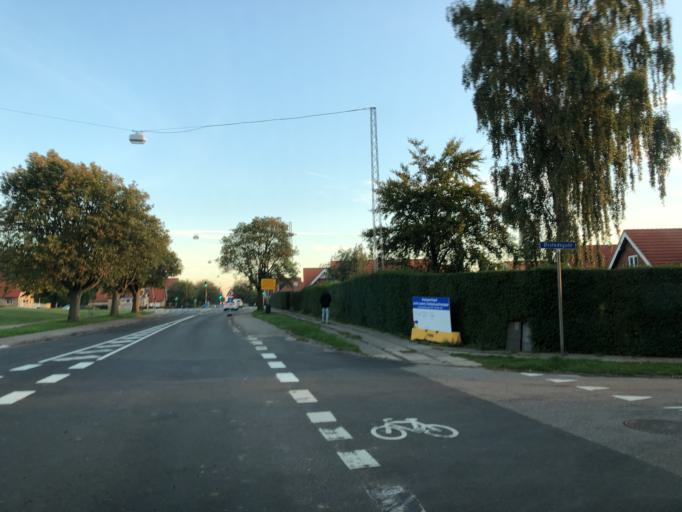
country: DK
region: South Denmark
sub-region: Sonderborg Kommune
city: Sonderborg
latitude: 54.9065
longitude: 9.8108
